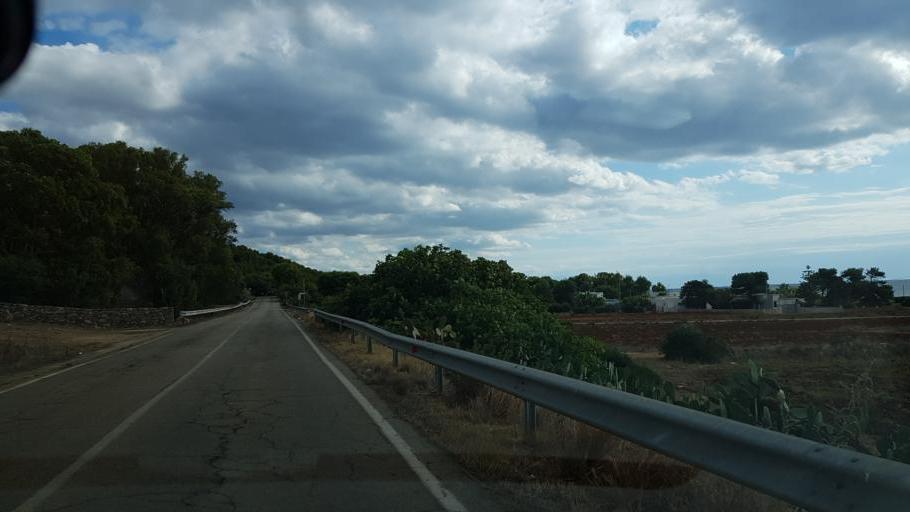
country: IT
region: Apulia
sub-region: Provincia di Lecce
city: Nardo
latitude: 40.1700
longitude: 17.9487
